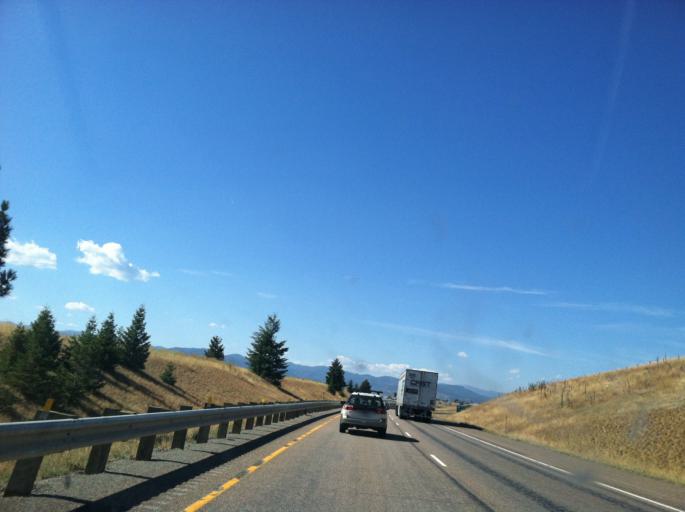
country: US
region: Montana
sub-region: Missoula County
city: Orchard Homes
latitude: 46.9390
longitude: -114.1063
